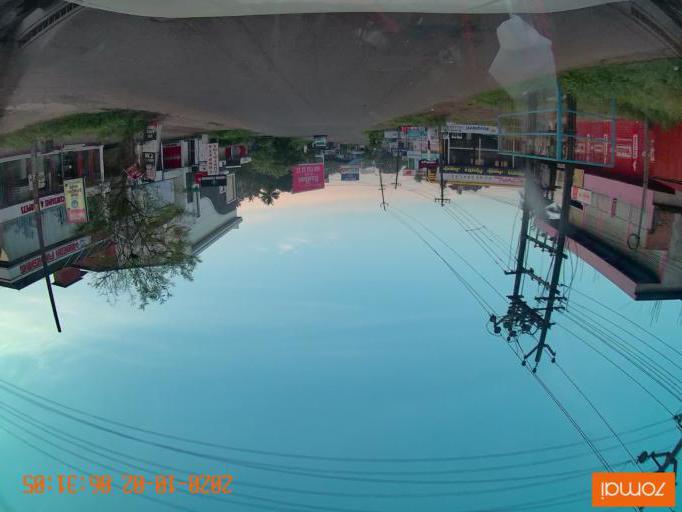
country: IN
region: Kerala
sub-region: Thrissur District
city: Kunnamkulam
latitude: 10.7386
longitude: 76.0292
